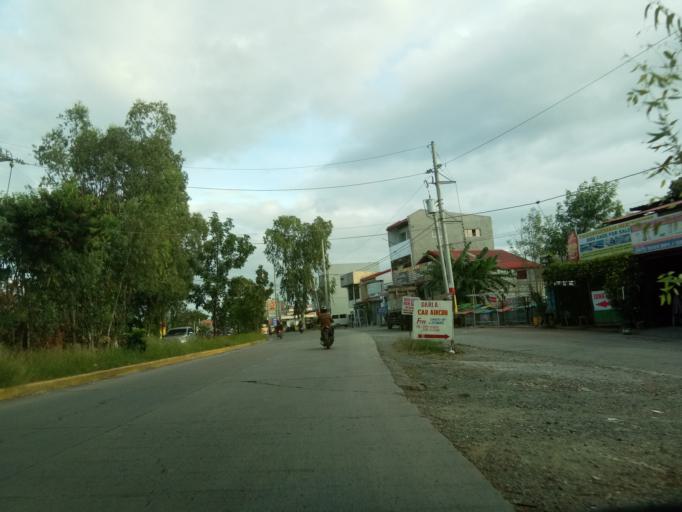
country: PH
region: Calabarzon
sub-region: Province of Cavite
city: Imus
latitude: 14.3882
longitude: 120.9701
